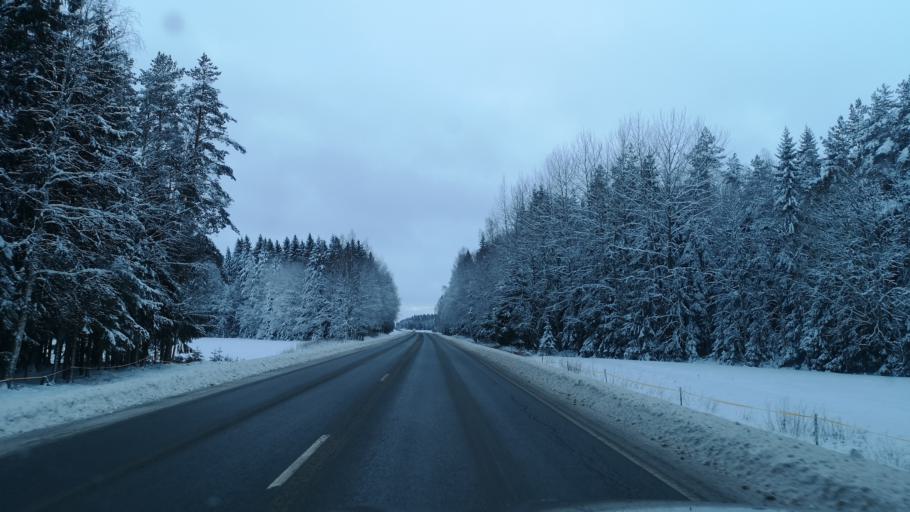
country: FI
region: Varsinais-Suomi
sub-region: Loimaa
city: Loimaa
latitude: 60.9106
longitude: 23.1697
